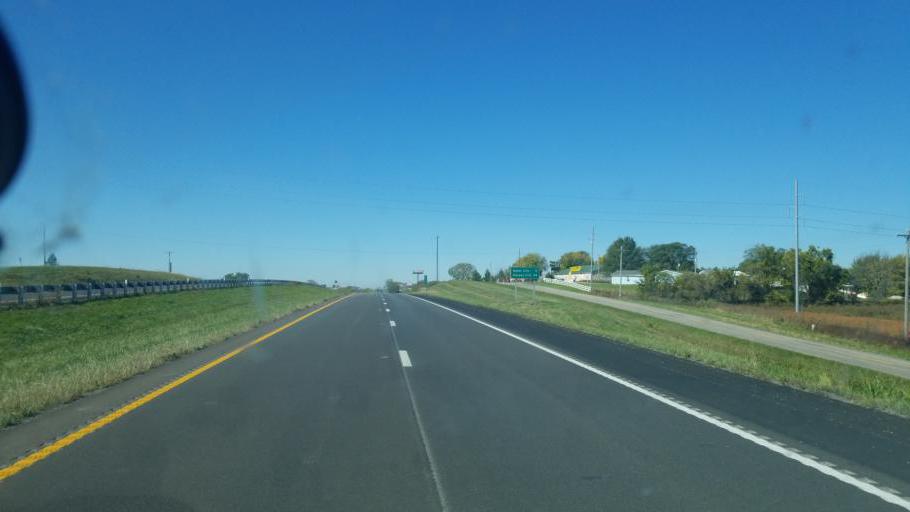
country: US
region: Missouri
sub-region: Lafayette County
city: Odessa
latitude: 39.0089
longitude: -93.9753
